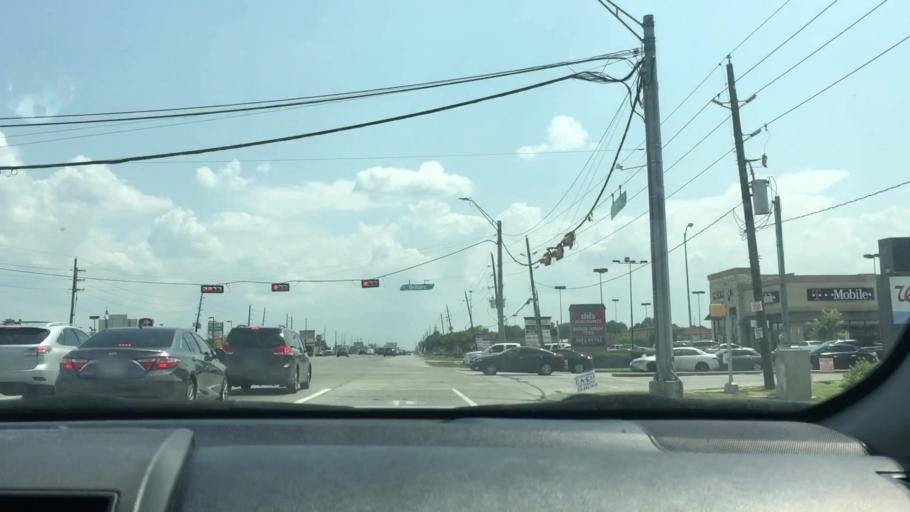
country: US
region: Texas
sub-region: Fort Bend County
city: Mission Bend
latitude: 29.7044
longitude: -95.6442
